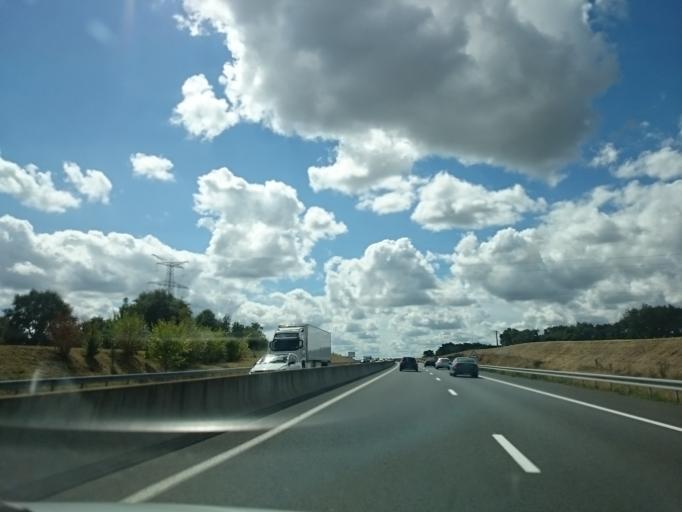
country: FR
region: Pays de la Loire
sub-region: Departement de Maine-et-Loire
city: Beaucouze
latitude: 47.4897
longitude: -0.6516
